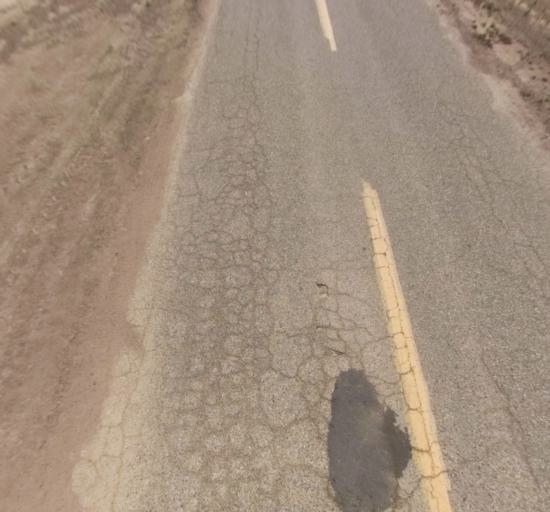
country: US
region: California
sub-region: Madera County
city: Fairmead
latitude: 37.0765
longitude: -120.2082
